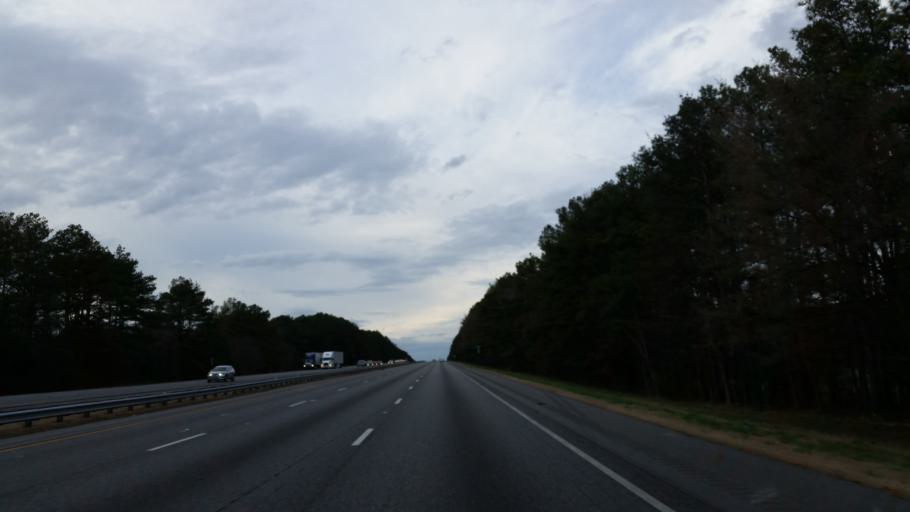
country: US
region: Georgia
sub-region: Bartow County
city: Adairsville
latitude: 34.3162
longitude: -84.8435
